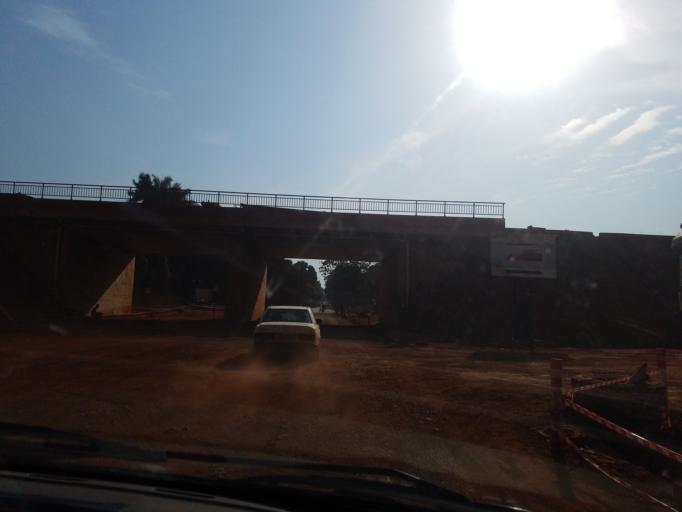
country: GN
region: Boke
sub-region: Boke Prefecture
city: Sangueya
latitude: 10.8119
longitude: -14.3841
